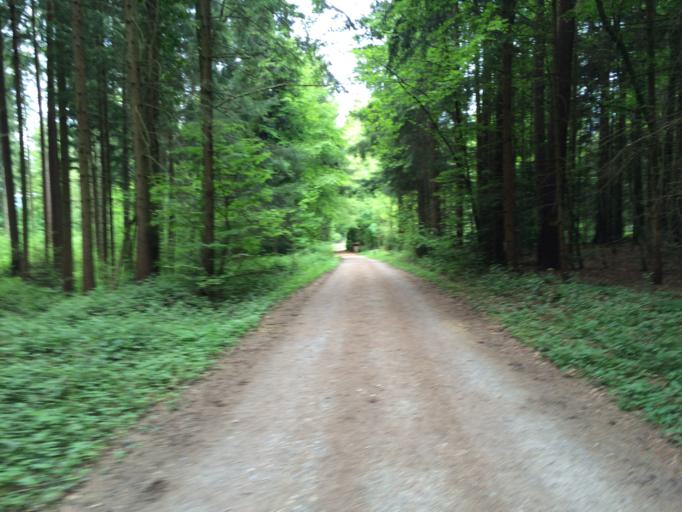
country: CH
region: Zurich
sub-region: Bezirk Uster
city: Uster / Ober-Uster
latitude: 47.3394
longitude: 8.7509
